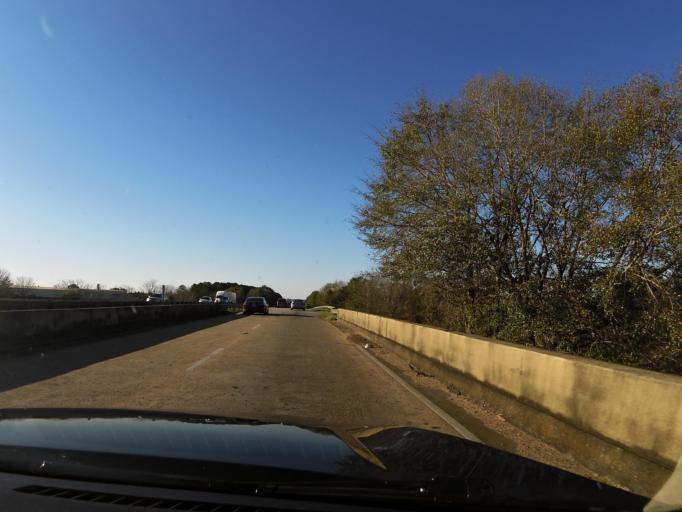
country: US
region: Alabama
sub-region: Dale County
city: Midland City
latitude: 31.3138
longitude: -85.5061
